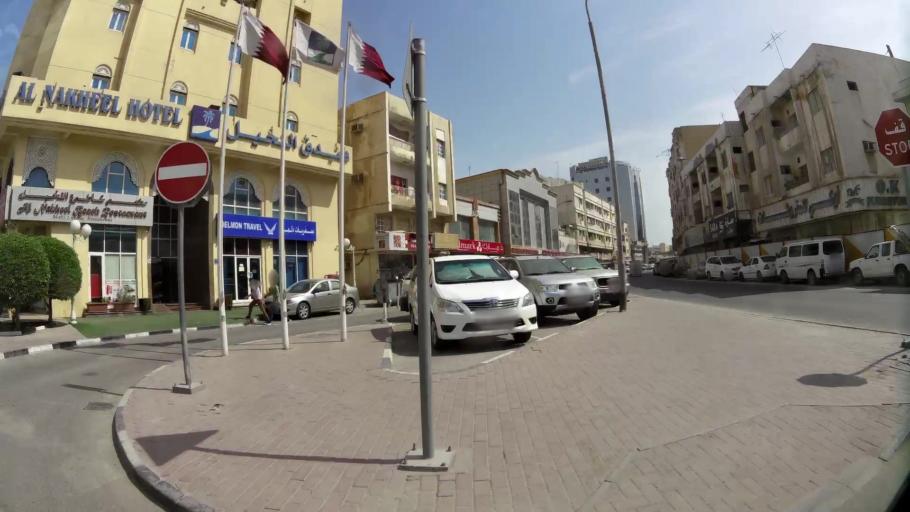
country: QA
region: Baladiyat ad Dawhah
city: Doha
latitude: 25.2843
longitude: 51.5322
